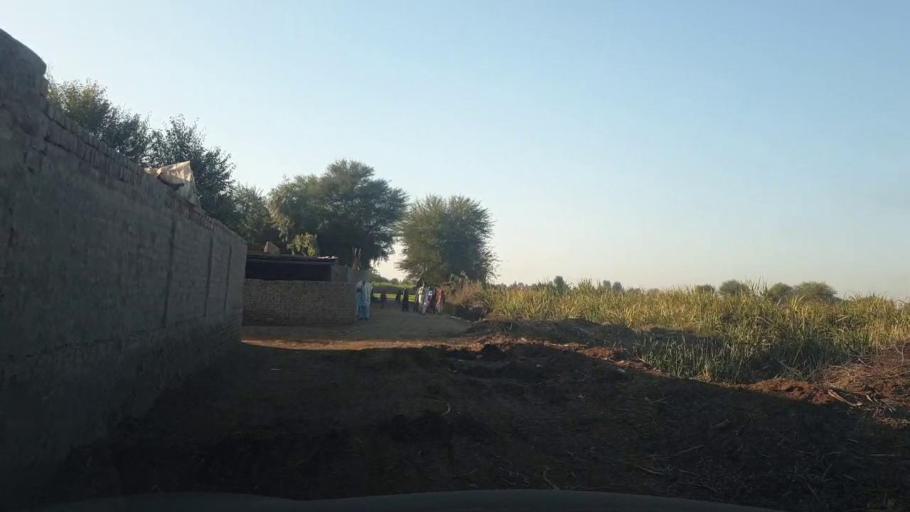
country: PK
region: Sindh
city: Ghotki
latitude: 28.0969
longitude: 69.3618
